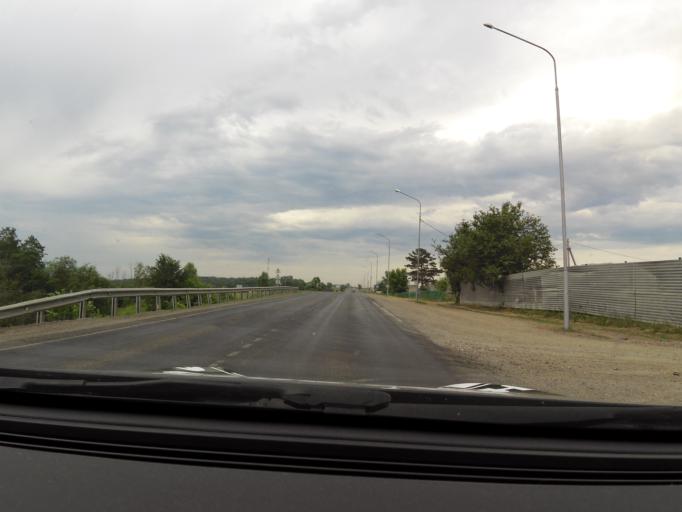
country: RU
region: Bashkortostan
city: Urman
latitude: 54.8250
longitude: 56.8914
